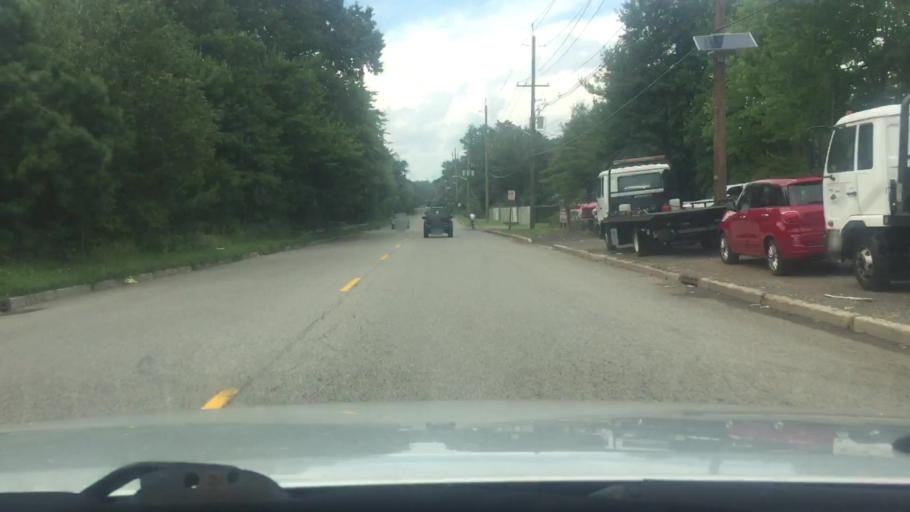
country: US
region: New Jersey
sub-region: Middlesex County
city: East Brunswick
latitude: 40.4490
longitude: -74.4088
